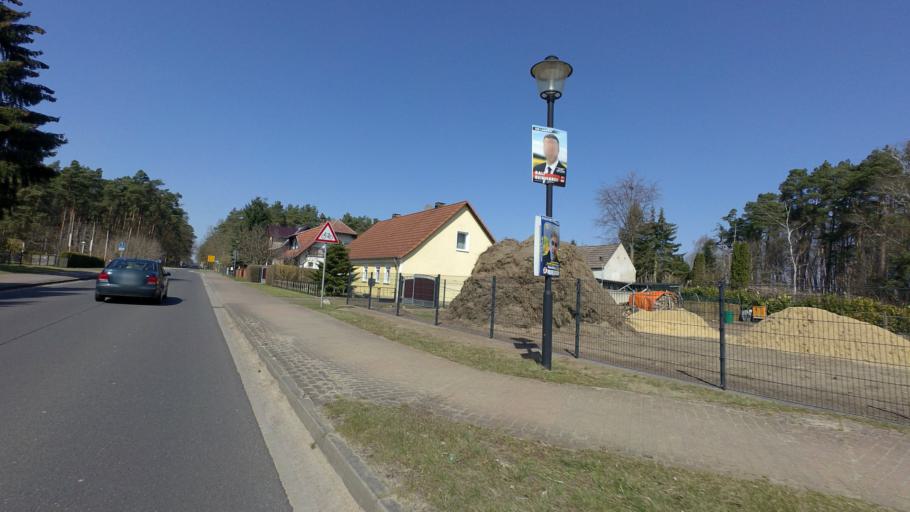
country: DE
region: Brandenburg
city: Ruthnick
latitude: 52.9073
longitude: 12.9598
